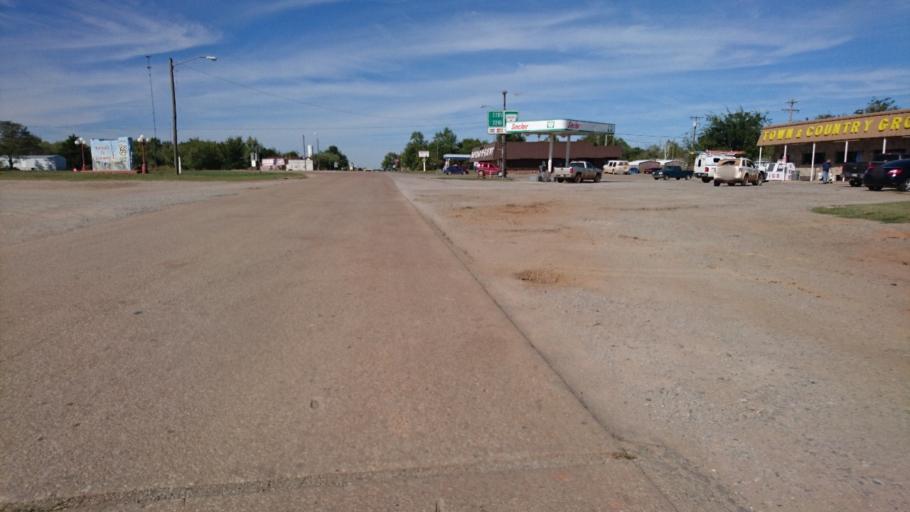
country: US
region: Oklahoma
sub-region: Lincoln County
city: Stroud
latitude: 35.7102
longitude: -96.7652
